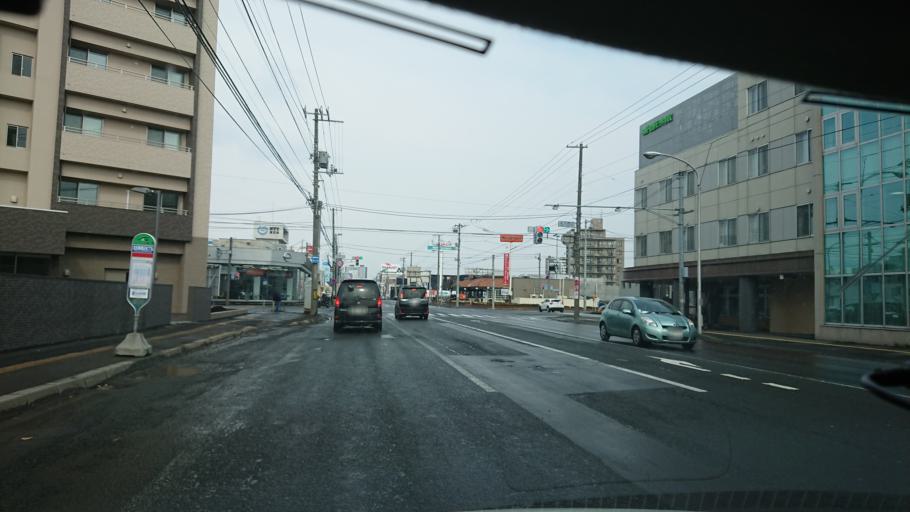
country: JP
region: Hokkaido
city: Sapporo
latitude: 43.0647
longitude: 141.3148
